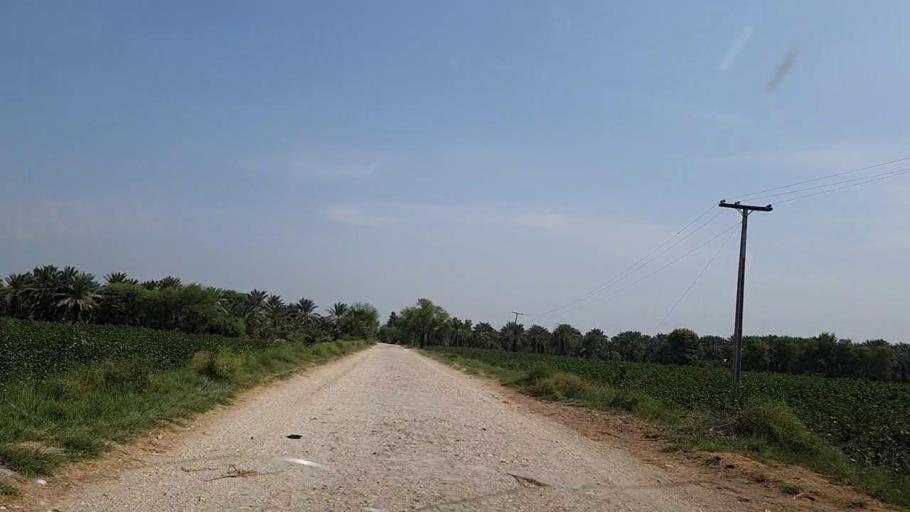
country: PK
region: Sindh
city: Khanpur
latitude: 27.7870
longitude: 69.3190
